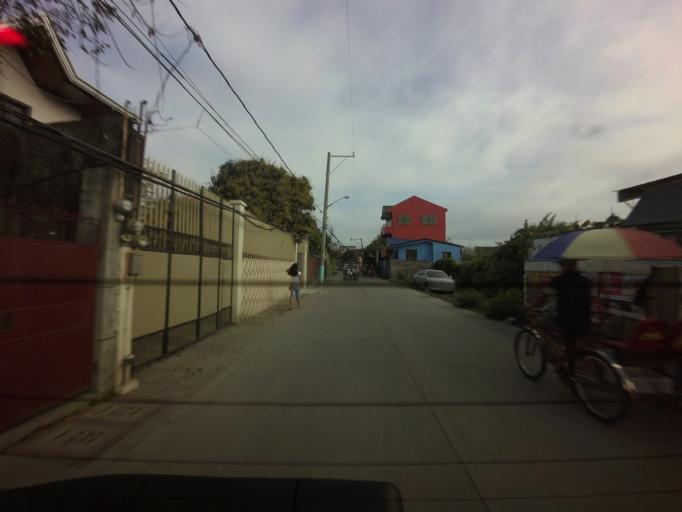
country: PH
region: Central Luzon
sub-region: Province of Bulacan
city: Obando
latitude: 14.7137
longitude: 120.9390
